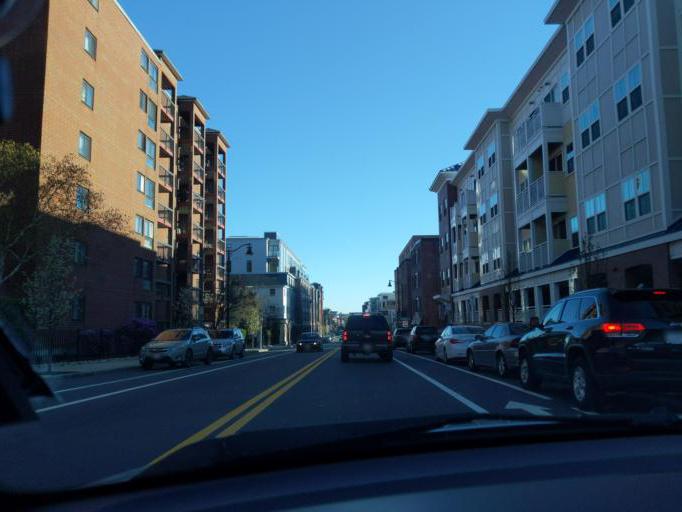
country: US
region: Massachusetts
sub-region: Essex County
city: Beverly
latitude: 42.5442
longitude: -70.8850
